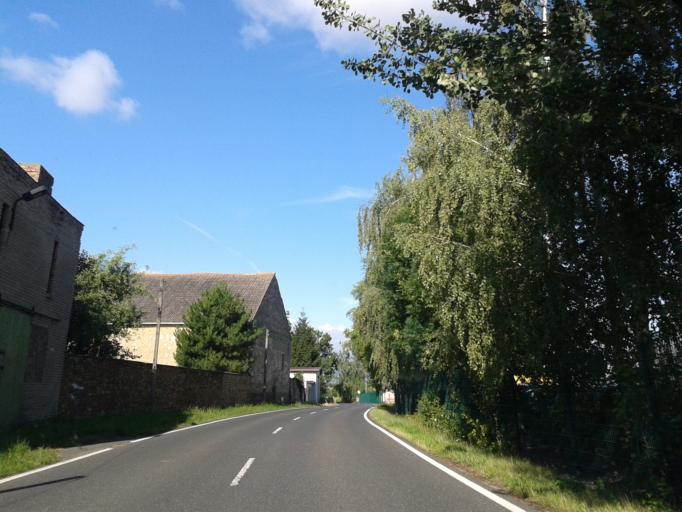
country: DE
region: Saxony-Anhalt
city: Peissen
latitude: 51.5099
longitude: 12.0350
